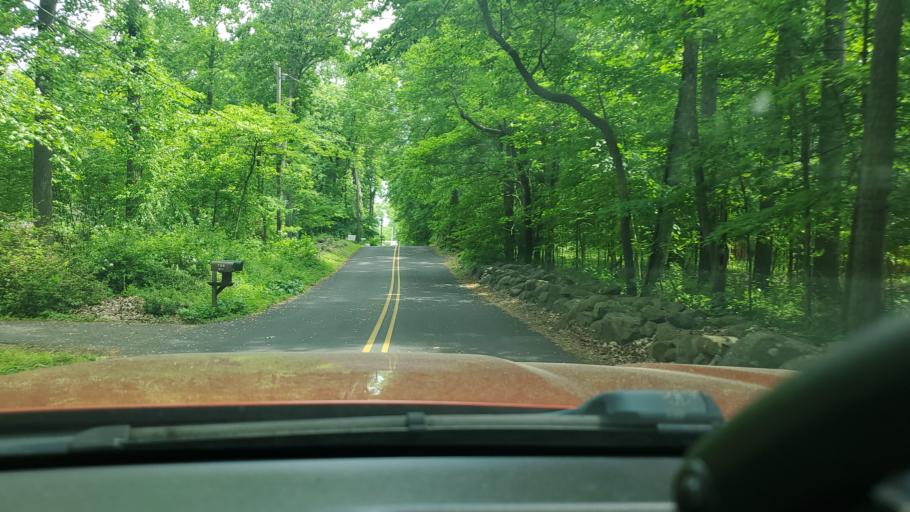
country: US
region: Pennsylvania
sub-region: Montgomery County
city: Red Hill
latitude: 40.3293
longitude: -75.5166
